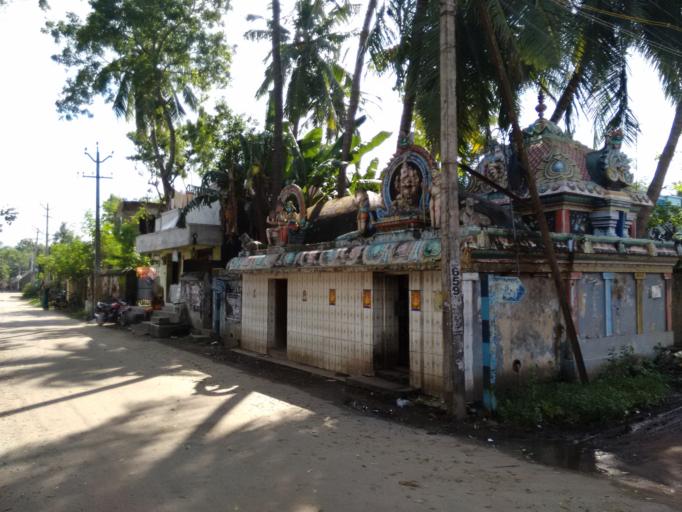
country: IN
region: Tamil Nadu
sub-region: Thiruvarur
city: Koradachcheri
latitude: 10.8493
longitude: 79.5140
